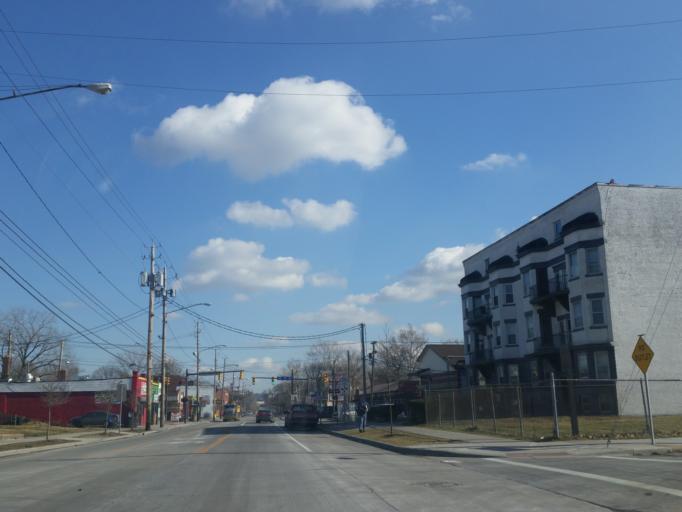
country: US
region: Ohio
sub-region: Cuyahoga County
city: Bratenahl
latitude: 41.5002
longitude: -81.6348
